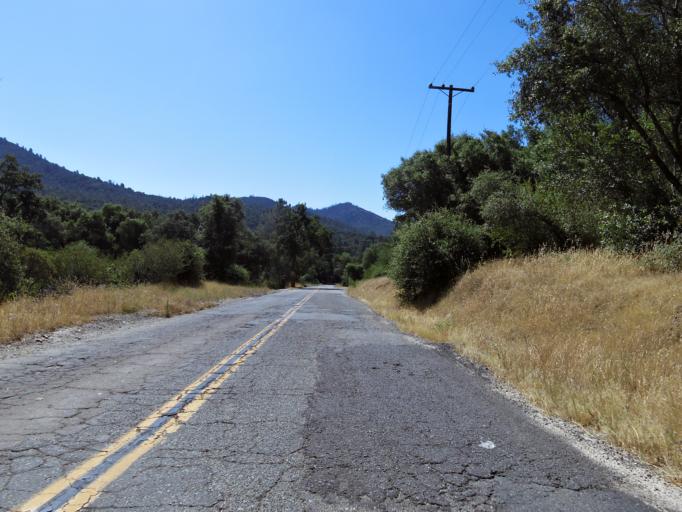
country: US
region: California
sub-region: Fresno County
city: Auberry
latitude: 37.2059
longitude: -119.4748
